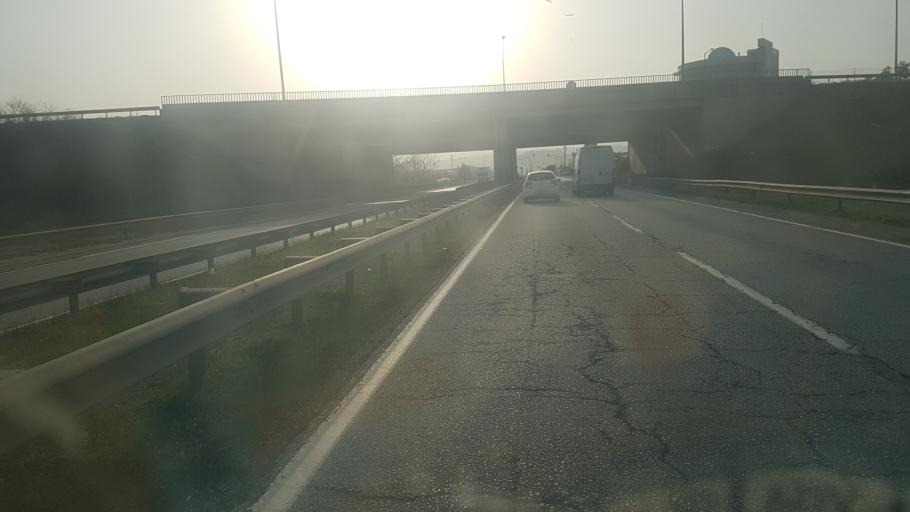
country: TR
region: Osmaniye
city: Toprakkale
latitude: 37.0628
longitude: 36.1091
